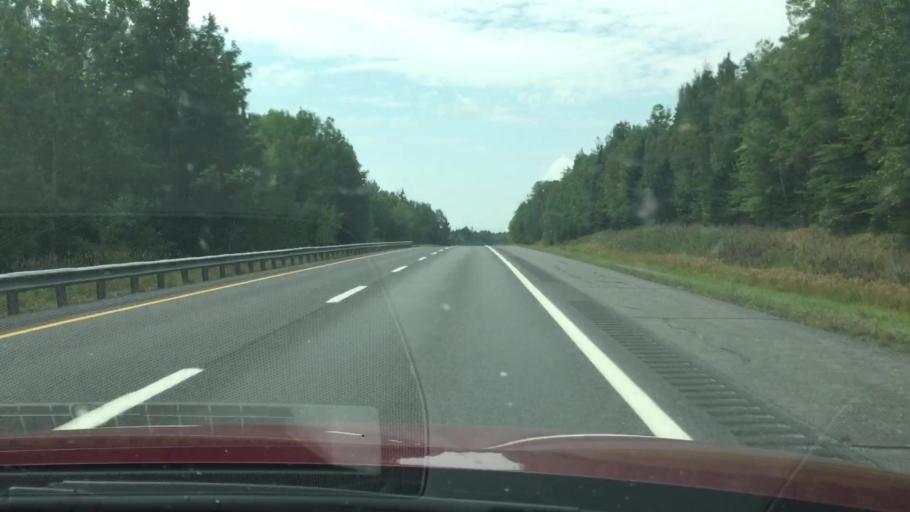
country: US
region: Maine
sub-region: Aroostook County
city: Hodgdon
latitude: 46.1264
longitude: -68.1035
